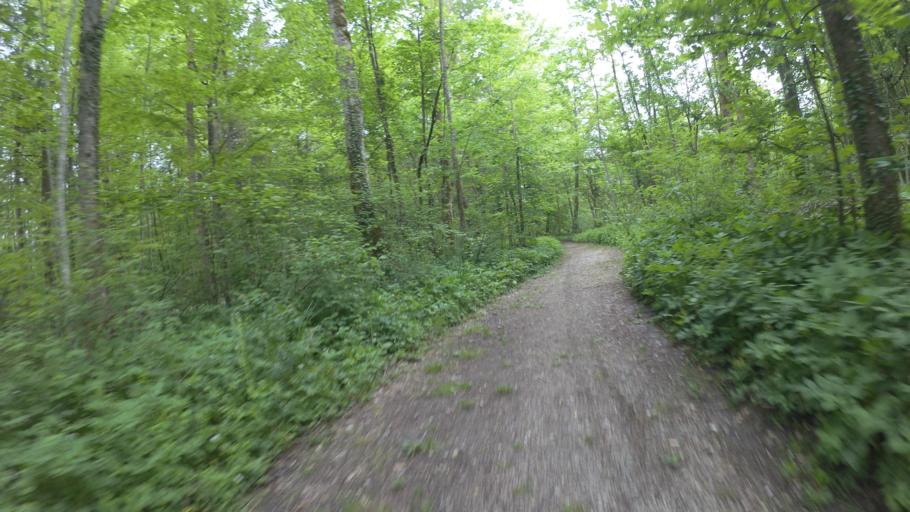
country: DE
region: Bavaria
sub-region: Upper Bavaria
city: Nussdorf
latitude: 47.9119
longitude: 12.6215
